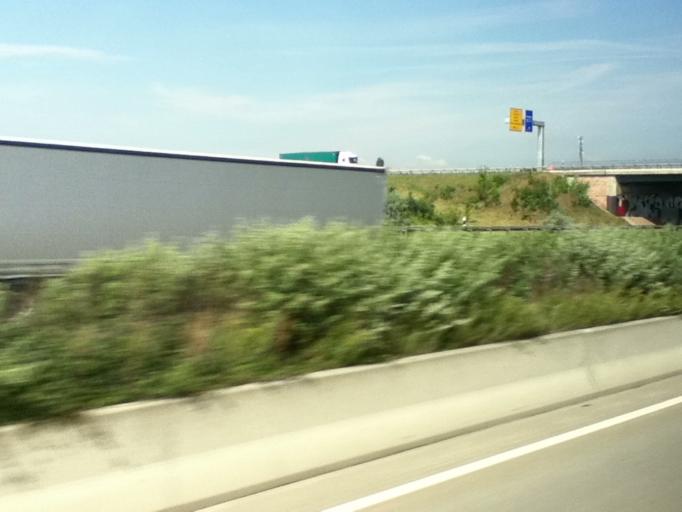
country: DE
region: Thuringia
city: Schwaara
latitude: 50.9024
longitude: 12.1278
